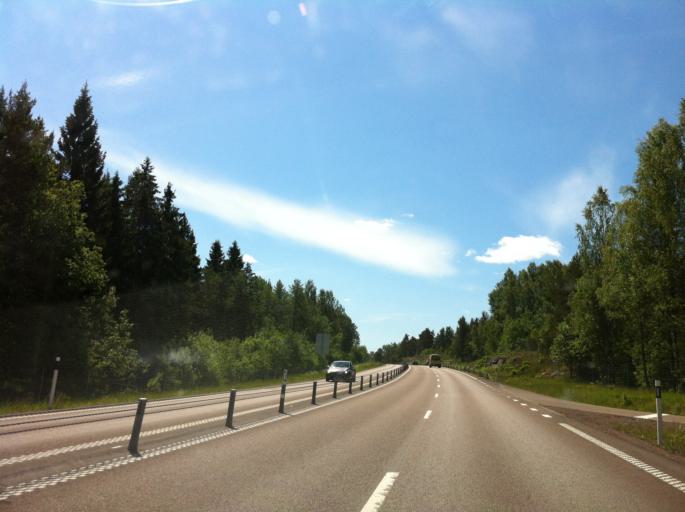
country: SE
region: Vaestra Goetaland
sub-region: Melleruds Kommun
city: Mellerud
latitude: 58.8231
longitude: 12.5240
